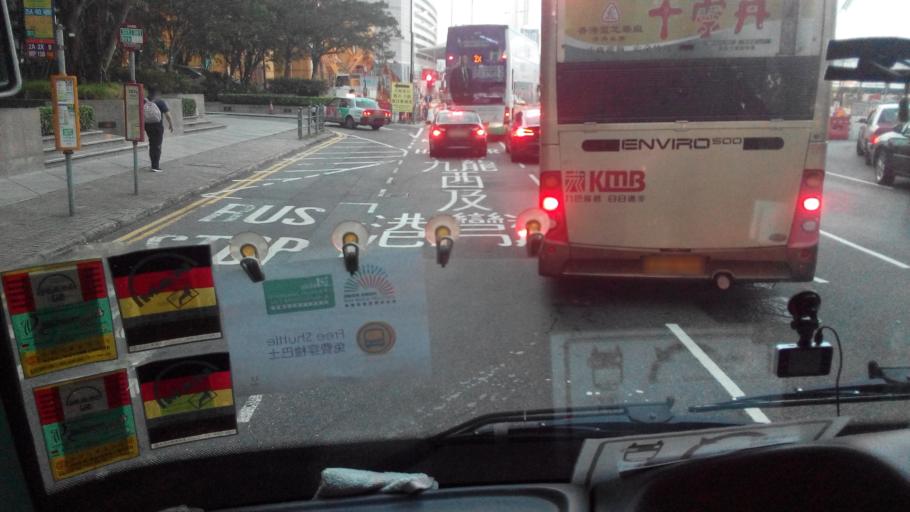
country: HK
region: Wanchai
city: Wan Chai
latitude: 22.2812
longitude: 114.1743
